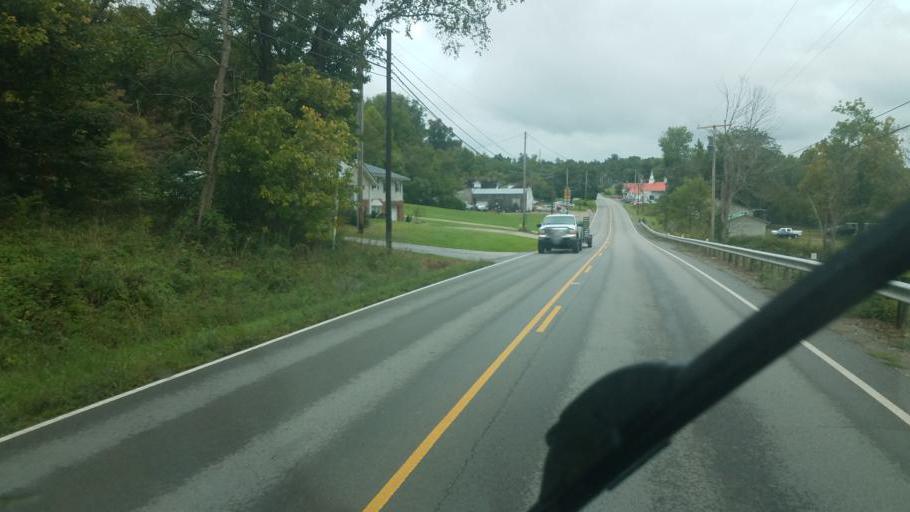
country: US
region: Ohio
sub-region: Scioto County
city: Sciotodale
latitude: 38.7653
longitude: -82.8447
